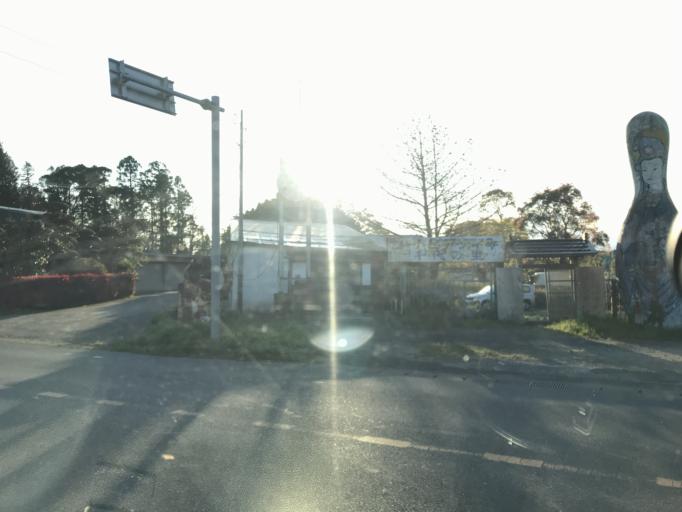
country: JP
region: Chiba
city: Yokaichiba
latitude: 35.7548
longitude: 140.5668
